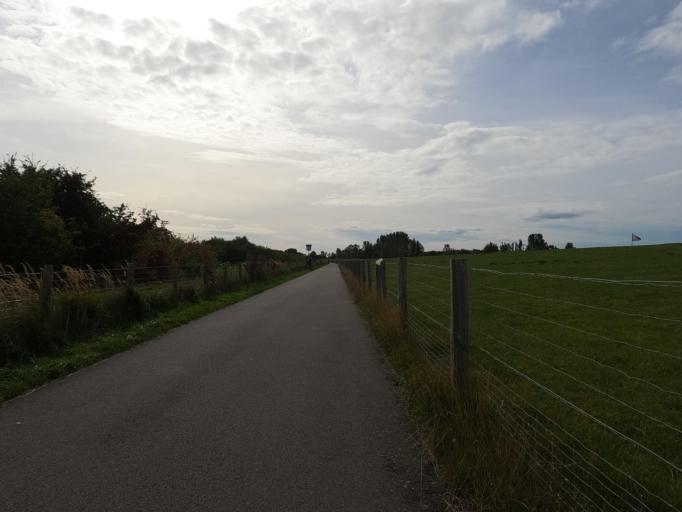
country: DE
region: Schleswig-Holstein
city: Dahme
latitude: 54.2436
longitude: 11.0809
